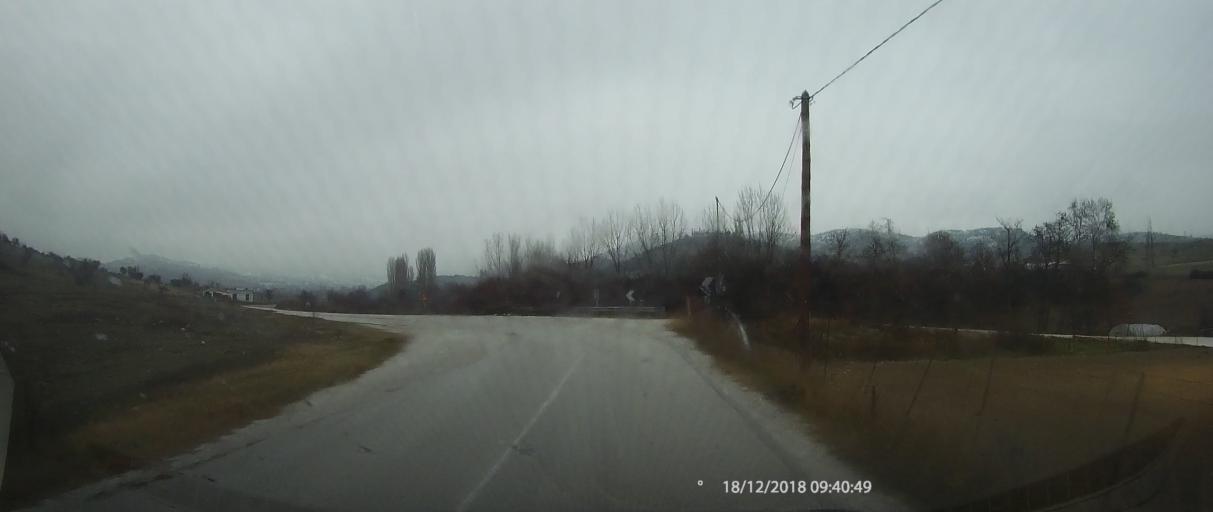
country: GR
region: Thessaly
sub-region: Nomos Larisis
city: Elassona
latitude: 40.0062
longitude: 22.2299
